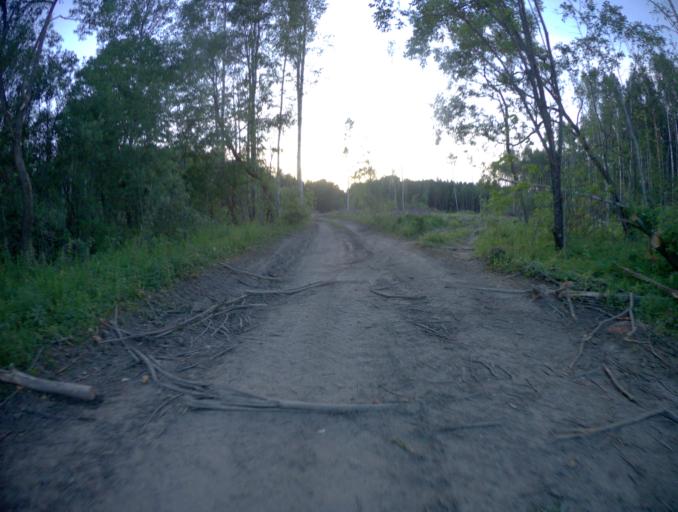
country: RU
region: Vladimir
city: Golovino
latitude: 56.0035
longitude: 40.4950
